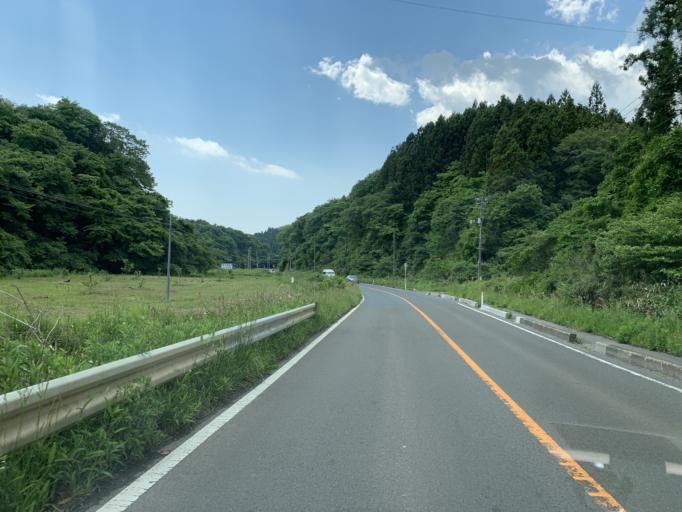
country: JP
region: Miyagi
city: Matsushima
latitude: 38.4137
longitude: 141.0634
